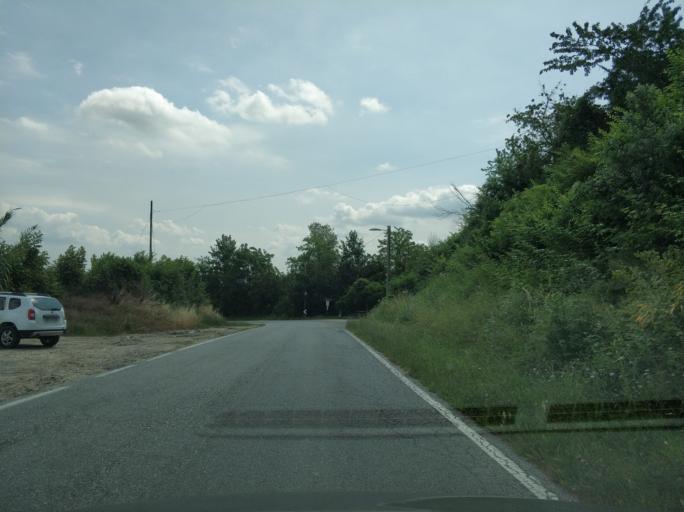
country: IT
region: Piedmont
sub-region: Provincia di Cuneo
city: Santo Stefano Roero
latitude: 44.7840
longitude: 7.9502
